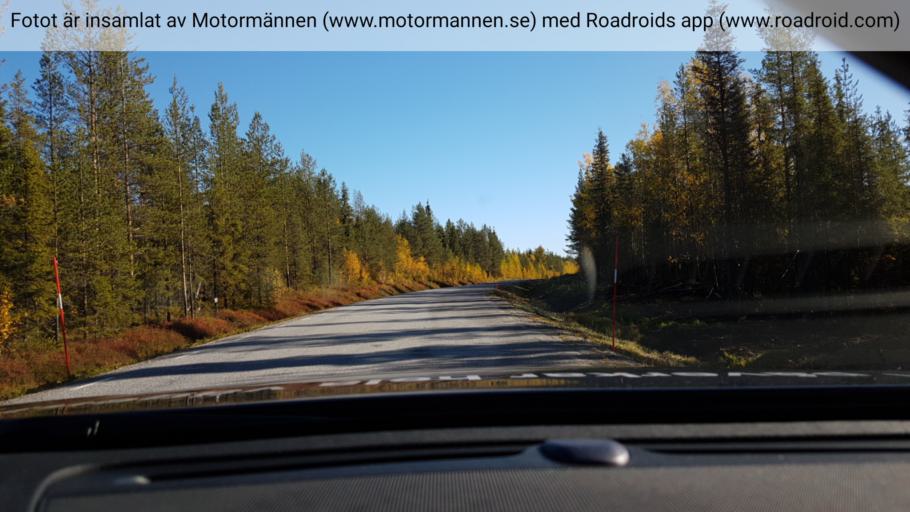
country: SE
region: Norrbotten
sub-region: Gallivare Kommun
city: Gaellivare
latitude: 66.4461
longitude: 20.7697
